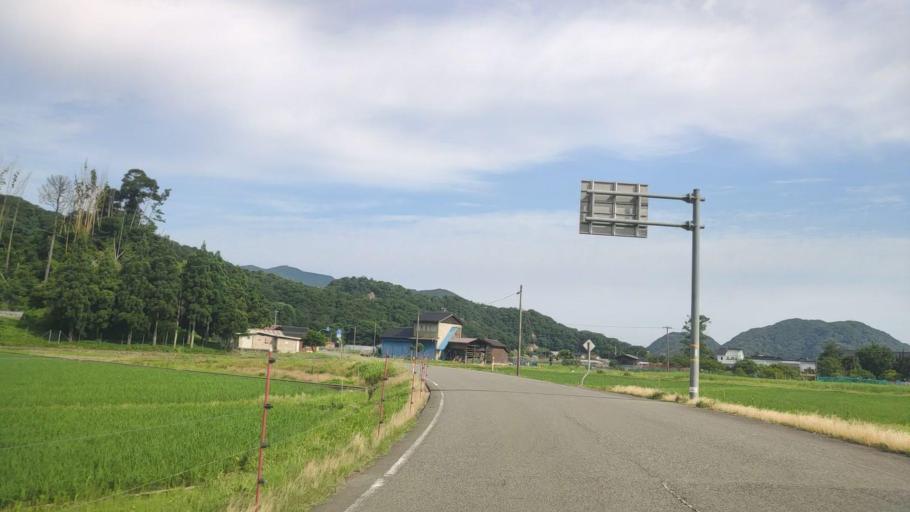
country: JP
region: Hyogo
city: Toyooka
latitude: 35.6324
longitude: 134.8406
